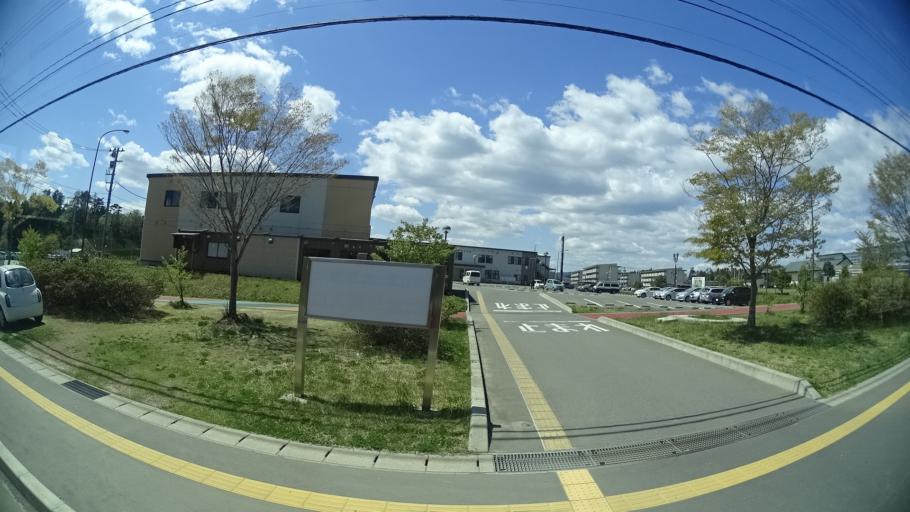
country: JP
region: Miyagi
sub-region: Oshika Gun
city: Onagawa Cho
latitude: 38.6797
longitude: 141.4617
